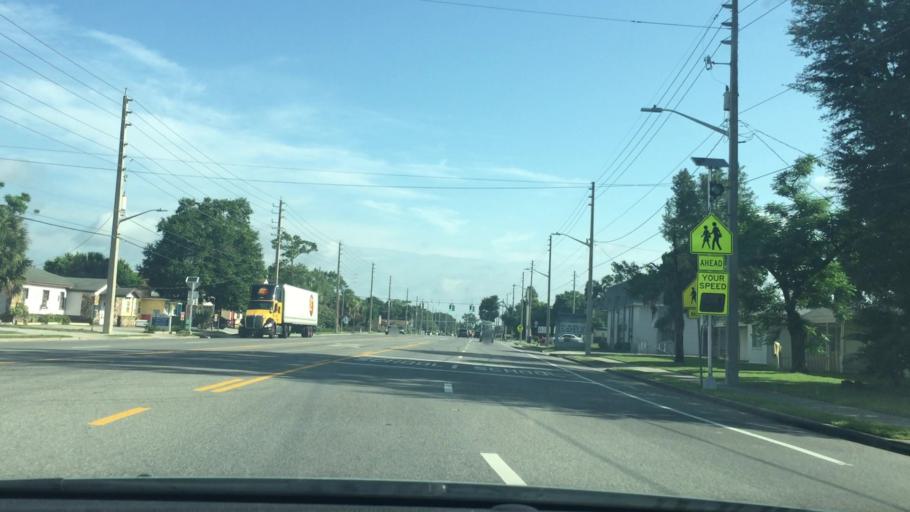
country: US
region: Florida
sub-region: Orange County
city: Pine Hills
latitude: 28.5659
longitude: -81.4515
